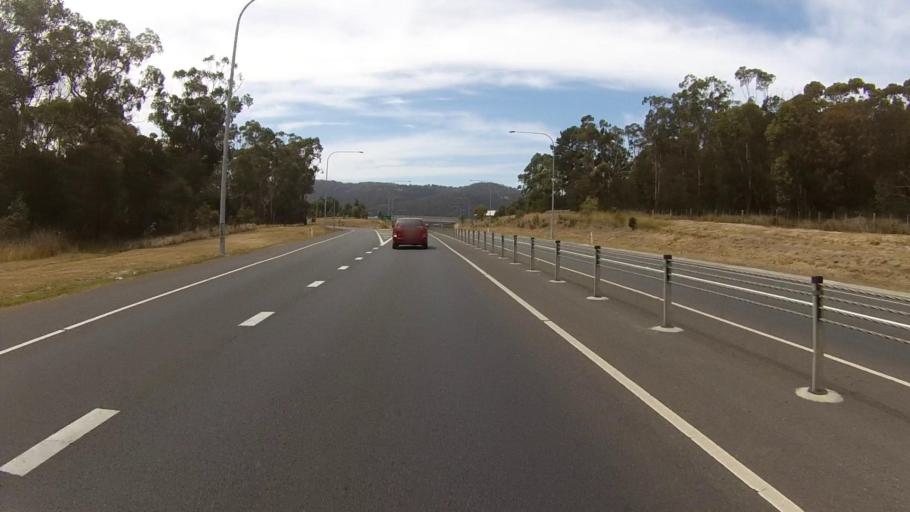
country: AU
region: Tasmania
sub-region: Kingborough
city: Kingston
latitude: -42.9777
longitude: 147.2982
